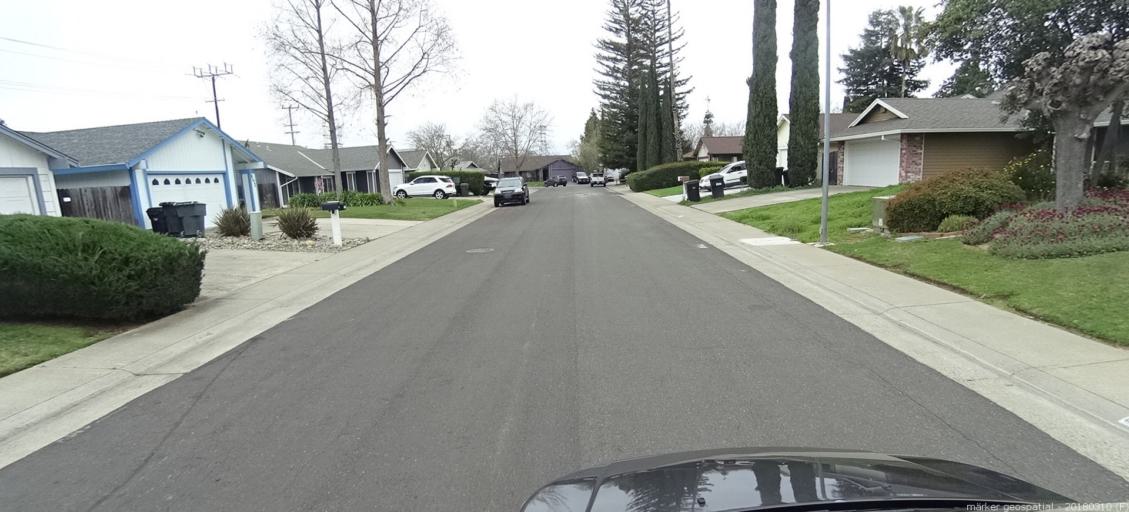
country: US
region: California
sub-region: Sacramento County
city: Florin
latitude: 38.4821
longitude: -121.4058
